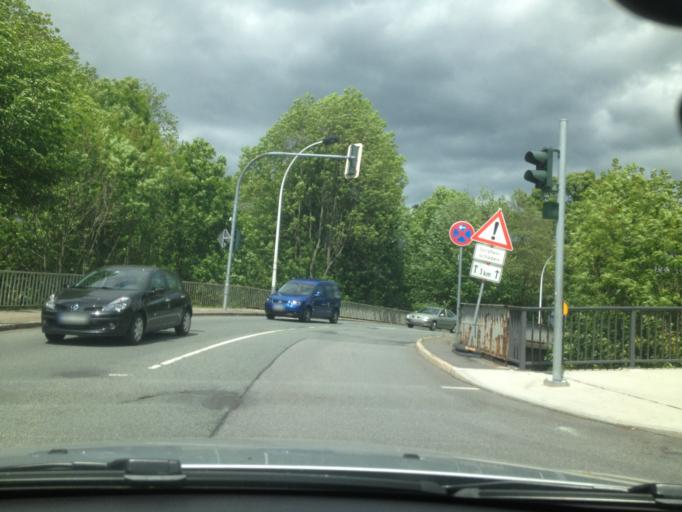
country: DE
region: Saxony
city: Annaberg-Buchholz
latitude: 50.5704
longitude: 12.9972
